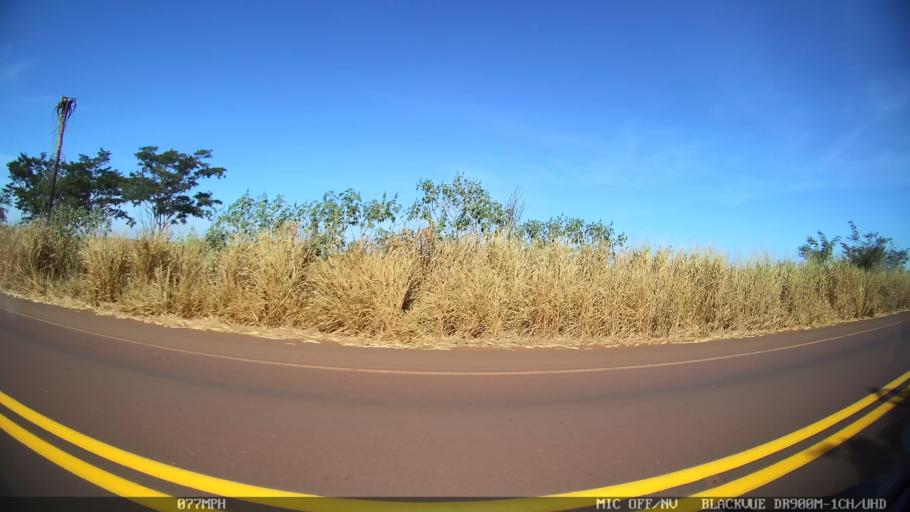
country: BR
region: Sao Paulo
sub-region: Barretos
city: Barretos
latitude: -20.4640
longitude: -48.4727
